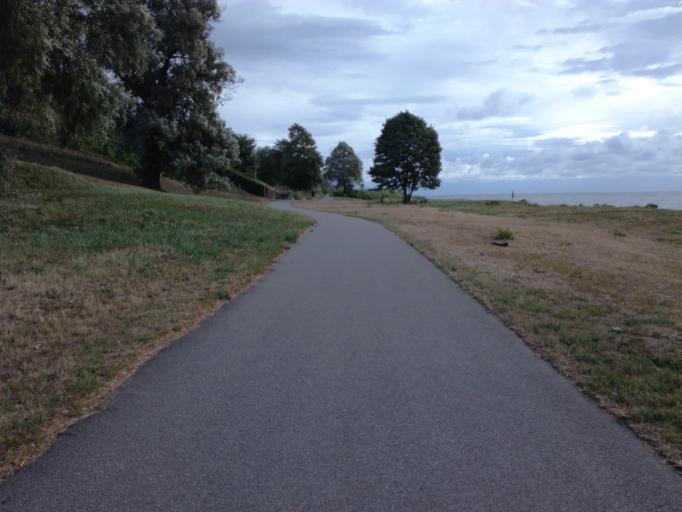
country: DK
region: South Denmark
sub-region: Fredericia Kommune
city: Fredericia
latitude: 55.5762
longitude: 9.7792
